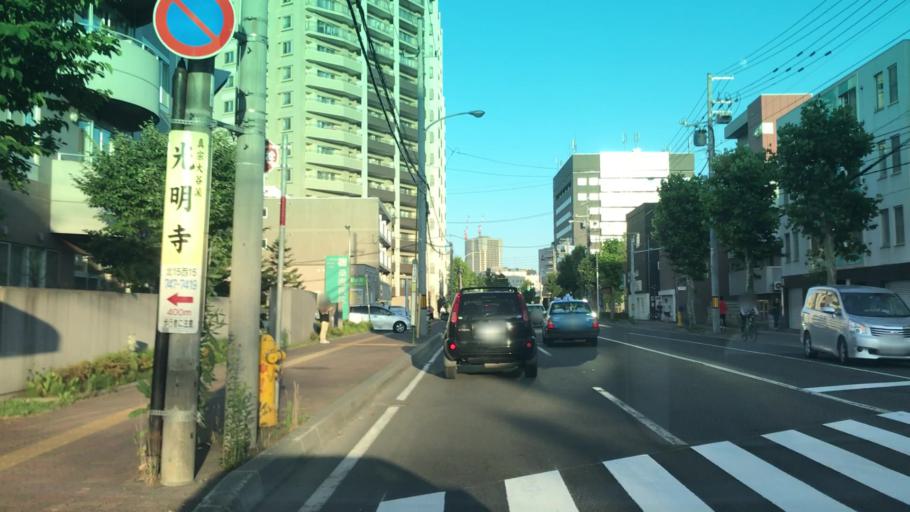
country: JP
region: Hokkaido
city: Sapporo
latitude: 43.0725
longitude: 141.3297
